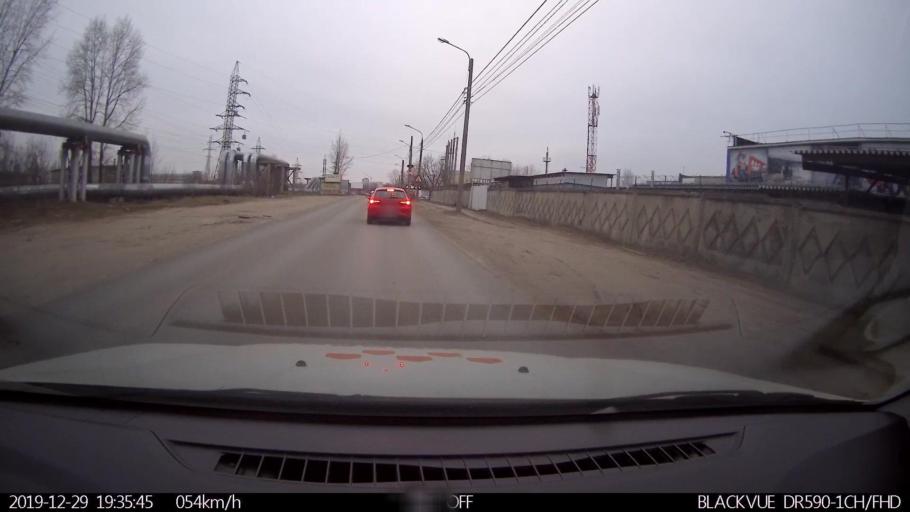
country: RU
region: Nizjnij Novgorod
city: Neklyudovo
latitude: 56.3485
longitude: 43.8925
